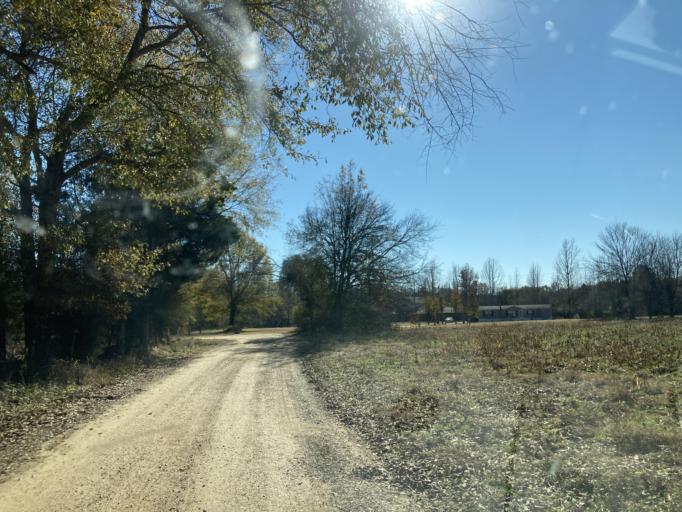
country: US
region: Mississippi
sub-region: Holmes County
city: Pickens
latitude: 32.8583
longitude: -90.0070
